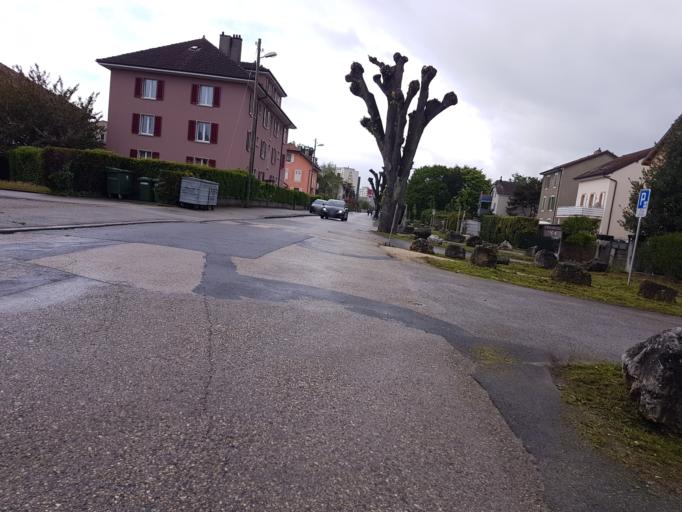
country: CH
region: Vaud
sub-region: Jura-Nord vaudois District
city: Yverdon-les-Bains
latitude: 46.7768
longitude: 6.6350
